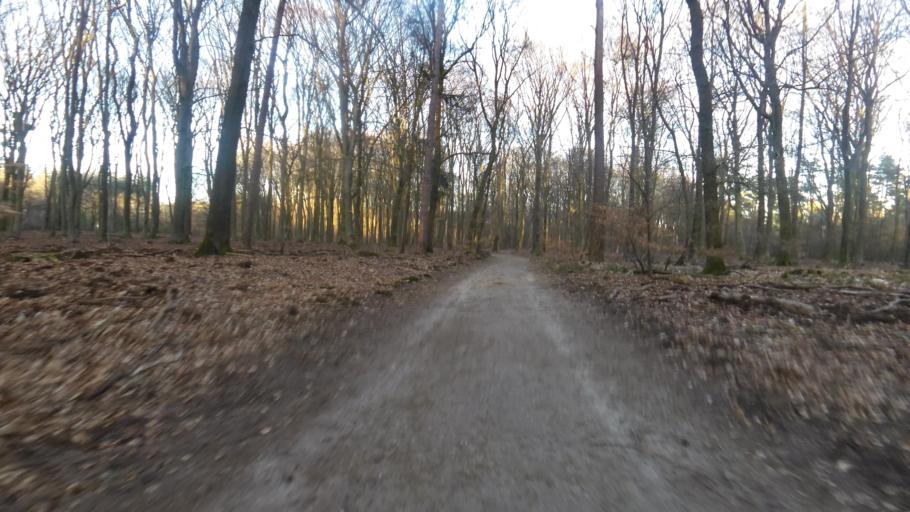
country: NL
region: Gelderland
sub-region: Gemeente Putten
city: Putten
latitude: 52.2475
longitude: 5.6559
